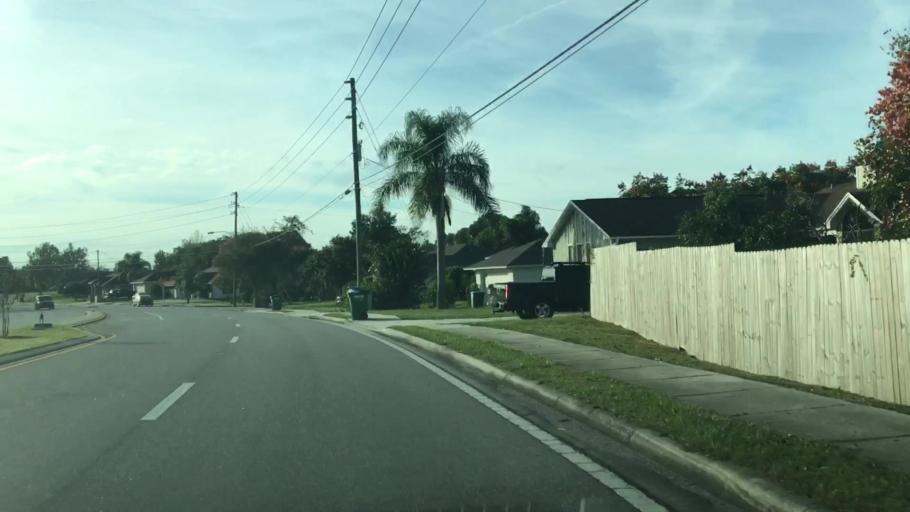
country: US
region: Florida
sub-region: Volusia County
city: Deltona
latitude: 28.9181
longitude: -81.2574
